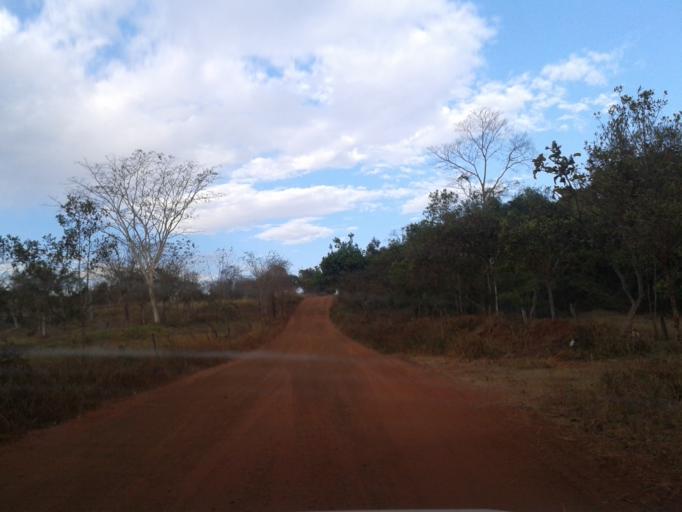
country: BR
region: Minas Gerais
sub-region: Ituiutaba
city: Ituiutaba
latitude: -19.1981
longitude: -49.8261
